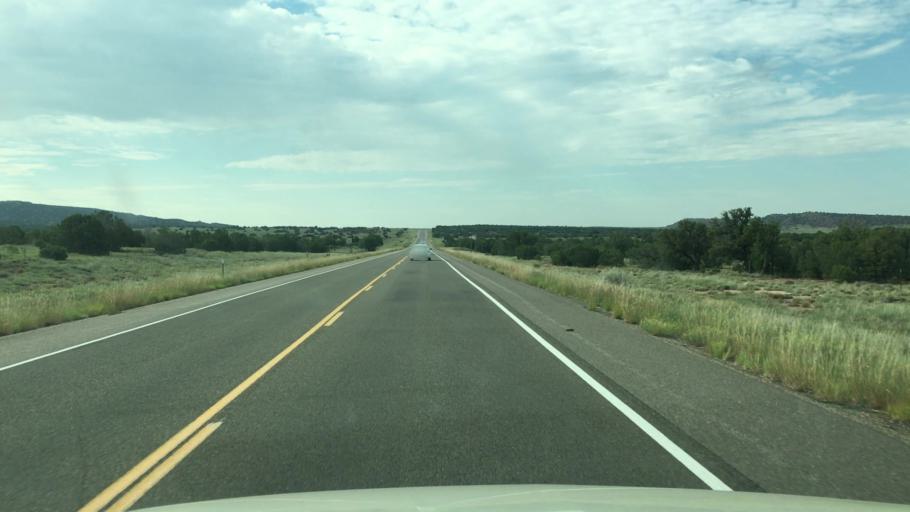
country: US
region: New Mexico
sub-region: Santa Fe County
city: Eldorado at Santa Fe
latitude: 35.3271
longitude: -105.8334
